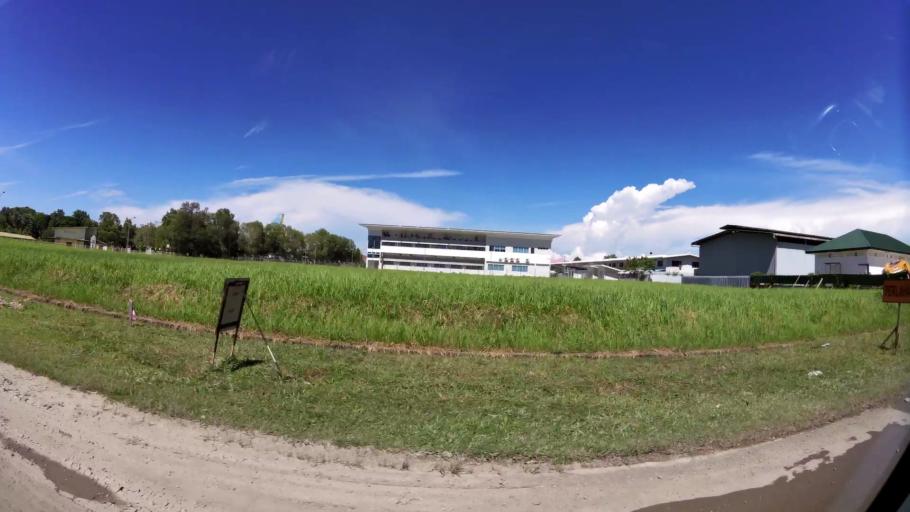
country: BN
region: Brunei and Muara
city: Bandar Seri Begawan
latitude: 5.0204
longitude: 115.0630
